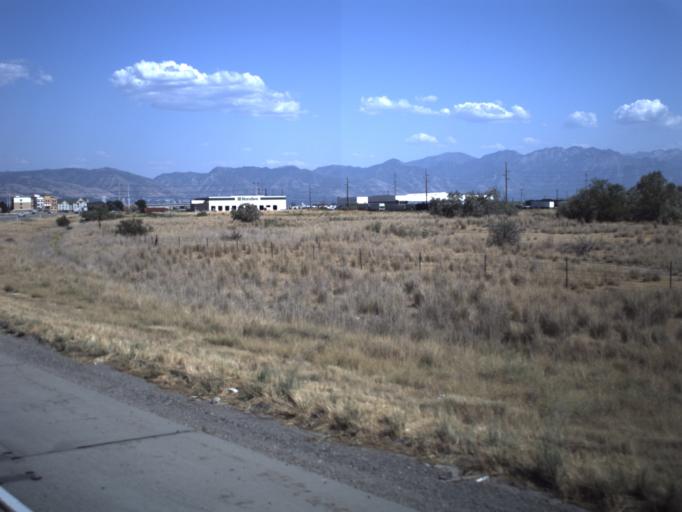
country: US
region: Utah
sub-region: Salt Lake County
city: West Valley City
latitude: 40.7706
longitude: -112.0204
